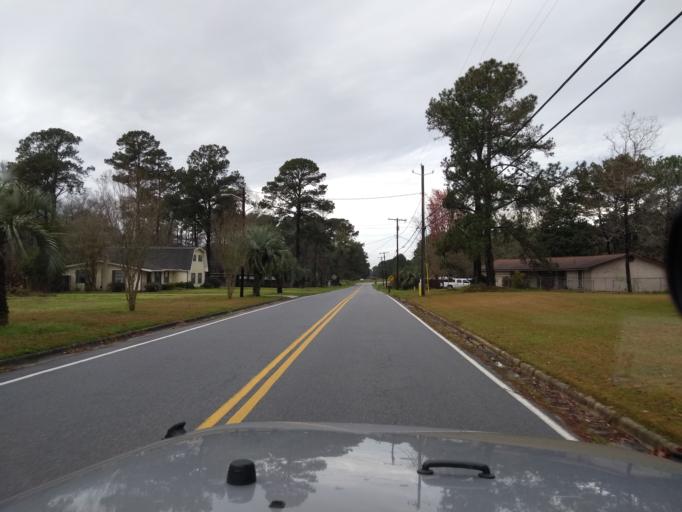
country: US
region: Georgia
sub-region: Chatham County
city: Georgetown
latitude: 32.0258
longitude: -81.1631
